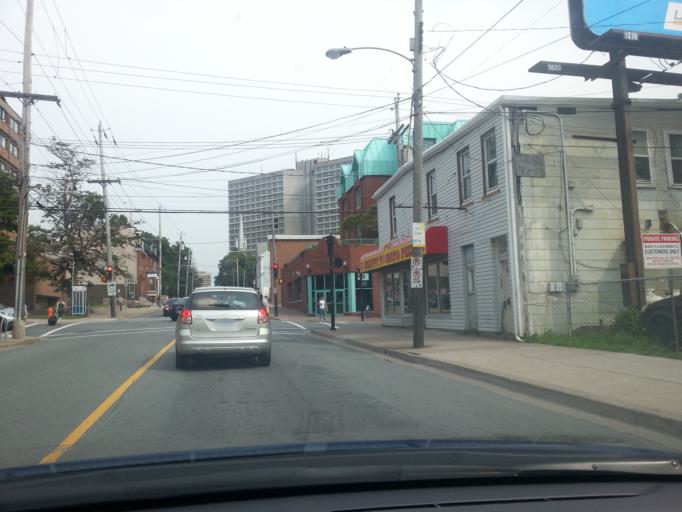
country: CA
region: Nova Scotia
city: Halifax
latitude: 44.6414
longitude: -63.5711
